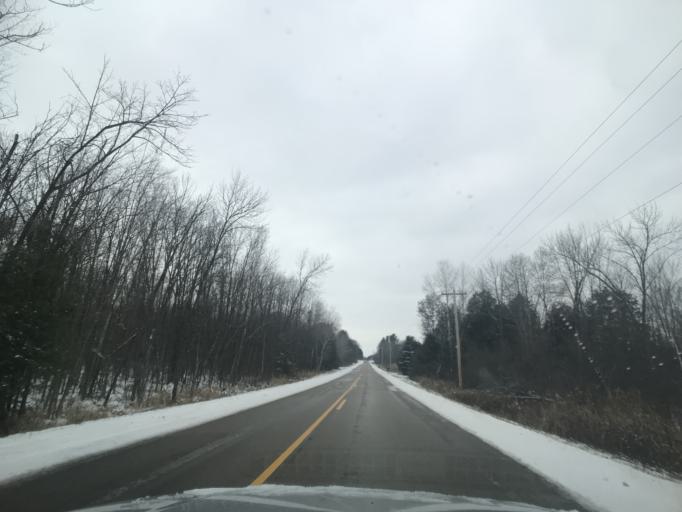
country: US
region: Wisconsin
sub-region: Brown County
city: Suamico
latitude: 44.7063
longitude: -88.0952
